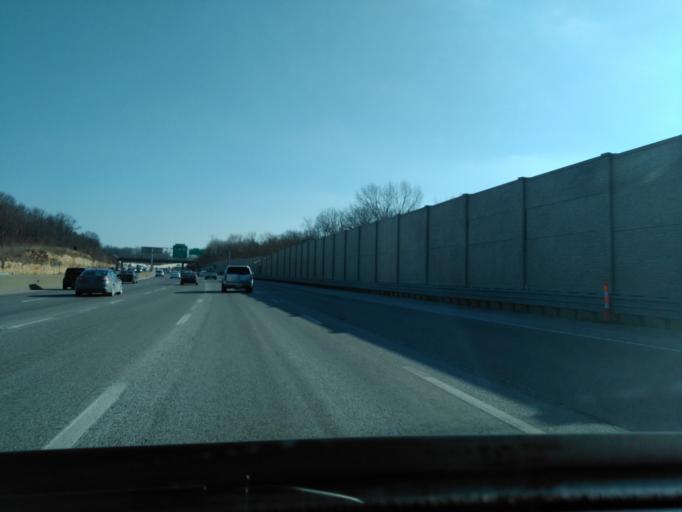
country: US
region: Missouri
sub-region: Saint Louis County
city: Des Peres
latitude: 38.5775
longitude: -90.4463
